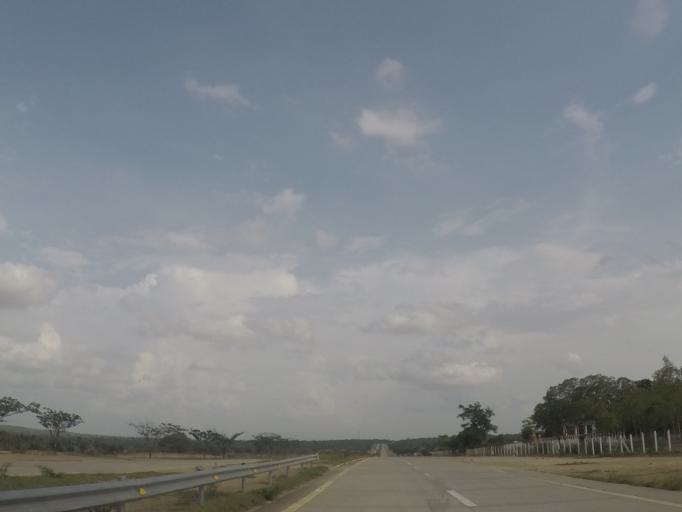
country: MM
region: Mandalay
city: Meiktila
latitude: 20.6616
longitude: 95.8030
